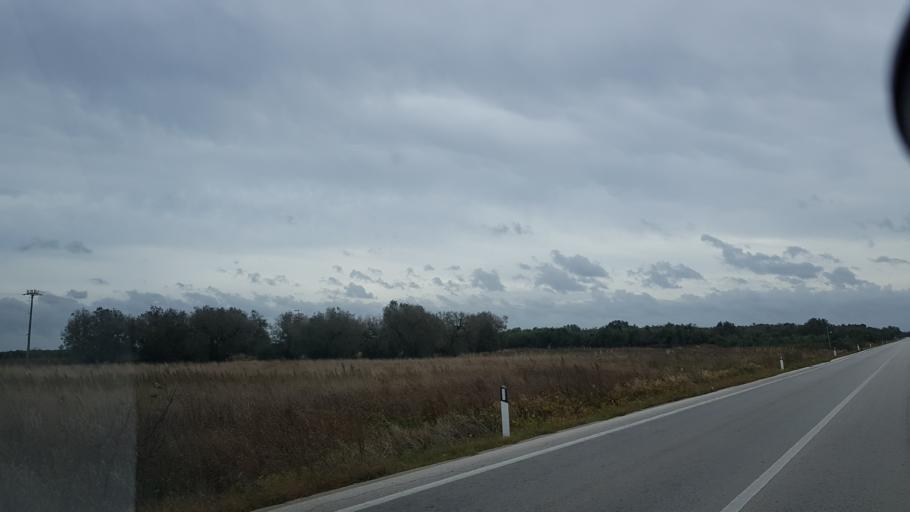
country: IT
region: Apulia
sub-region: Provincia di Lecce
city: Guagnano
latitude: 40.4015
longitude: 17.9097
